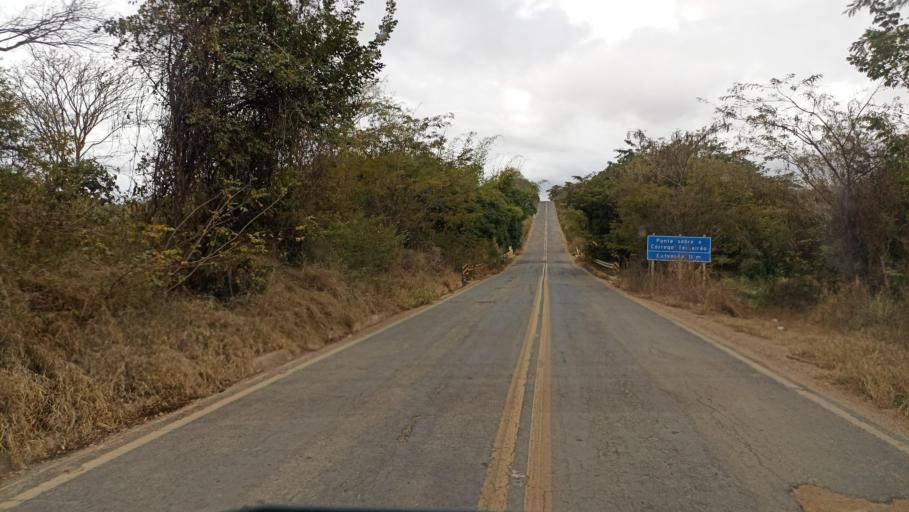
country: BR
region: Minas Gerais
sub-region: Itinga
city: Itinga
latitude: -16.6400
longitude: -41.8149
